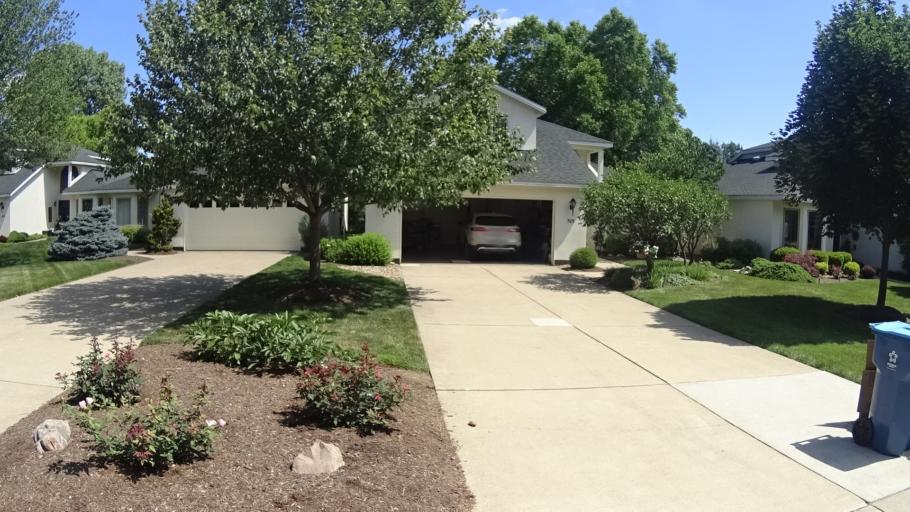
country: US
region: Ohio
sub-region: Erie County
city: Huron
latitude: 41.3769
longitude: -82.5650
